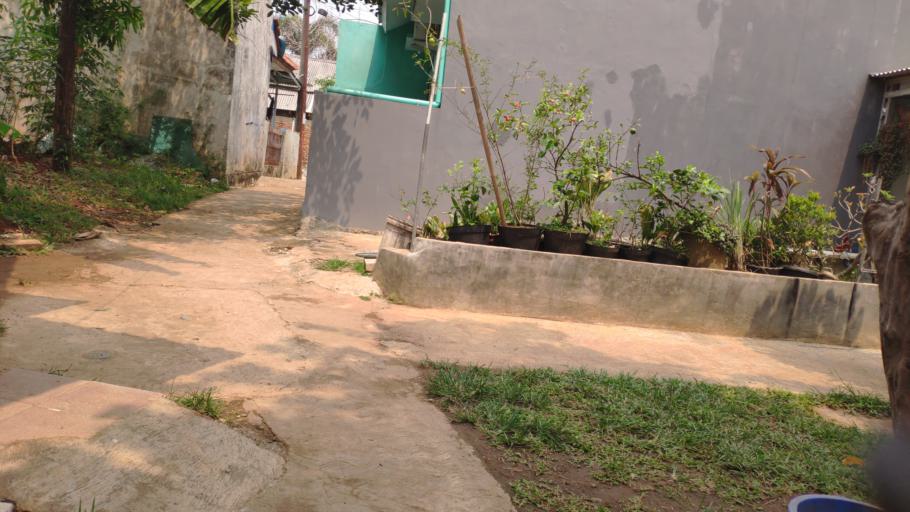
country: ID
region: West Java
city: Depok
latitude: -6.3689
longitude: 106.8071
